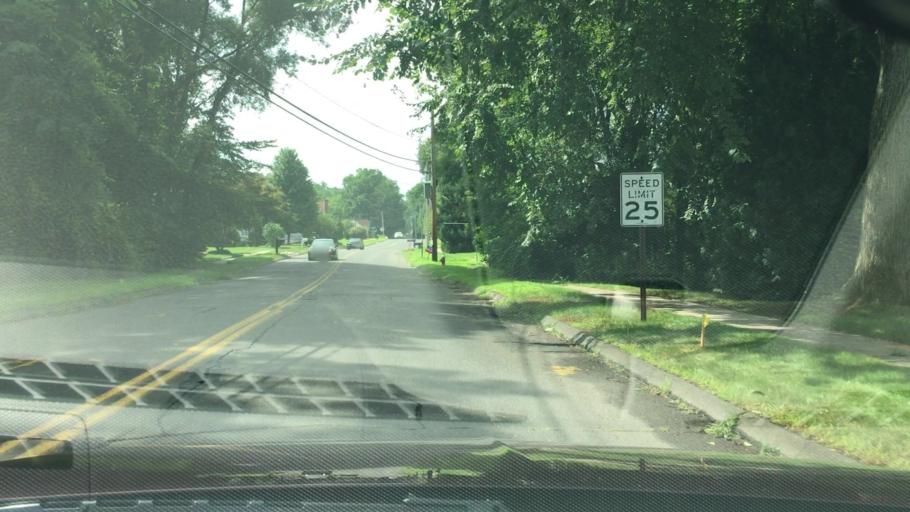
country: US
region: Connecticut
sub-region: Hartford County
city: Kensington
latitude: 41.6244
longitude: -72.7670
